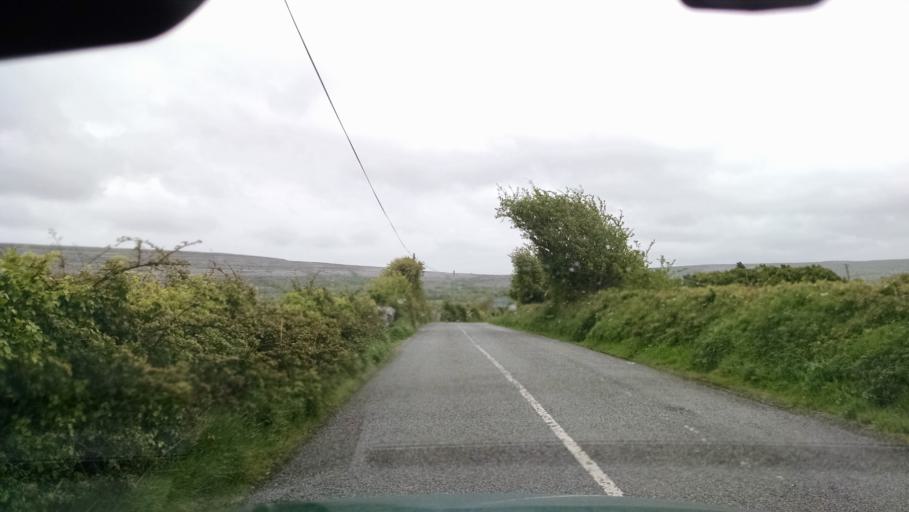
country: IE
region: Connaught
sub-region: County Galway
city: Bearna
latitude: 53.1025
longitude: -9.1595
